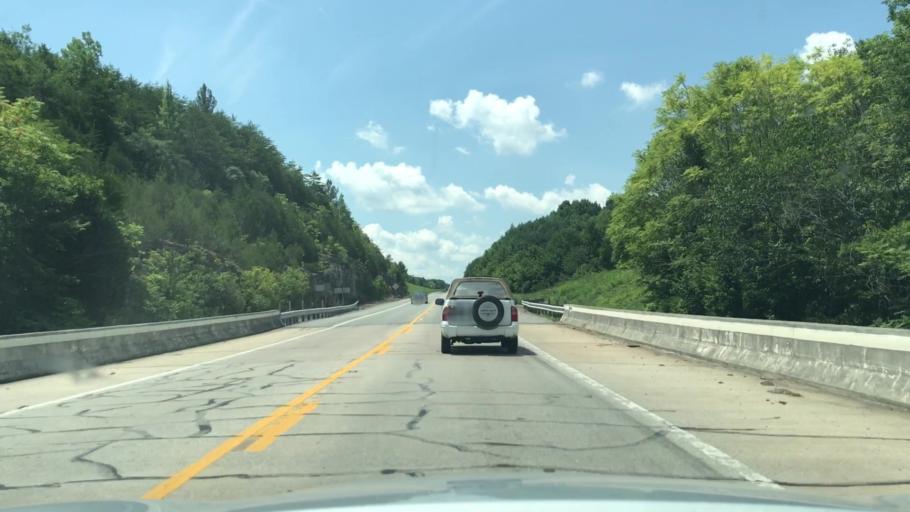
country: US
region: Tennessee
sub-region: Pickett County
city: Byrdstown
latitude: 36.6015
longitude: -85.1209
